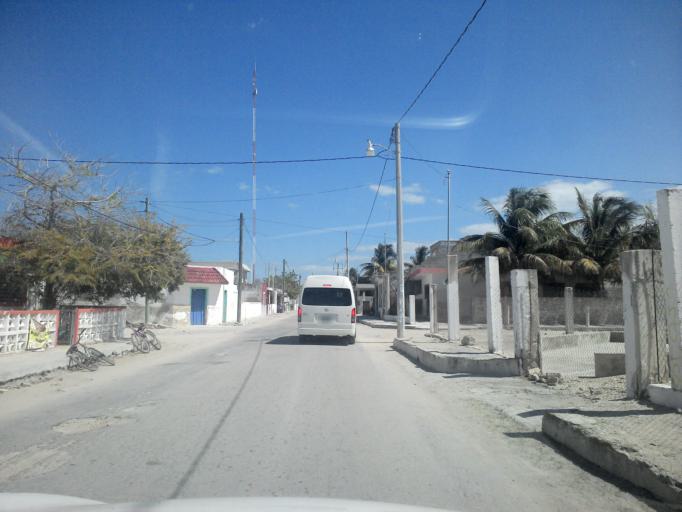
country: MX
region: Yucatan
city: Telchac Puerto
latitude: 21.3419
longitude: -89.2663
